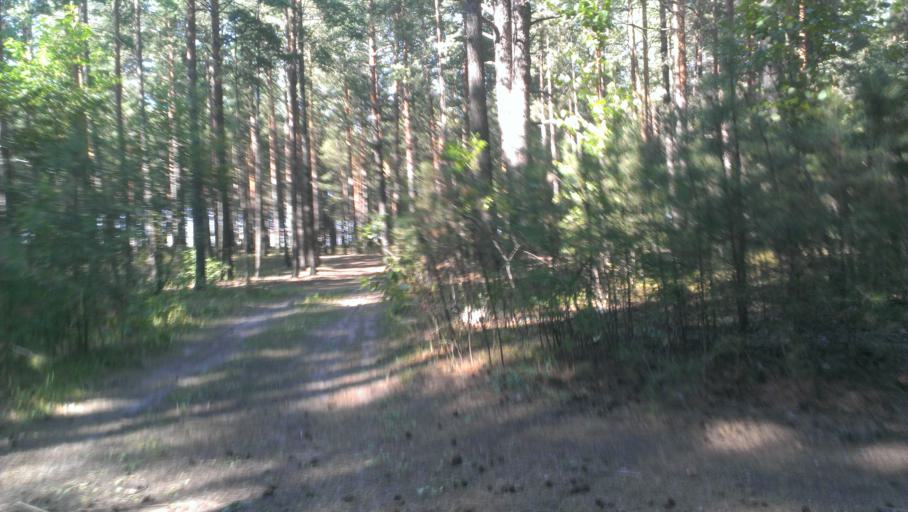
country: RU
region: Altai Krai
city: Novosilikatnyy
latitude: 53.3170
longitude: 83.6836
